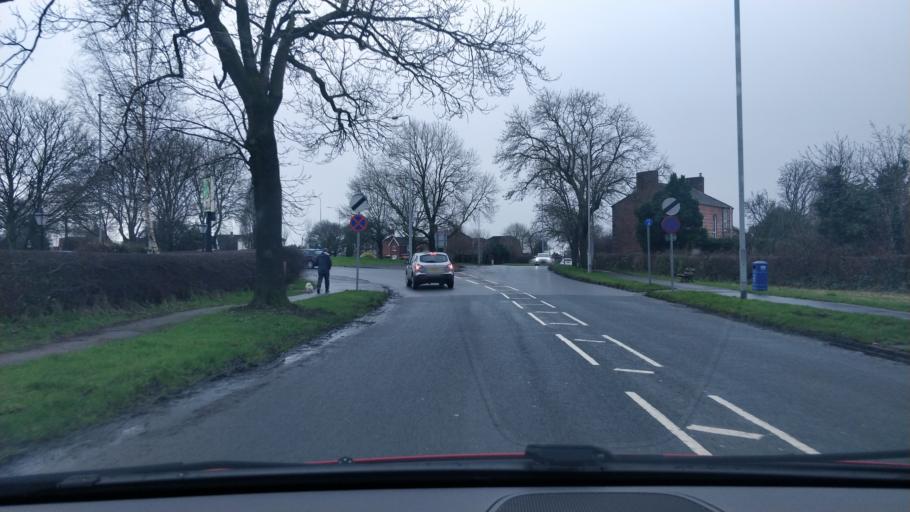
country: GB
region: England
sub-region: Lancashire
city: Tarleton
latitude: 53.7079
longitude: -2.7942
